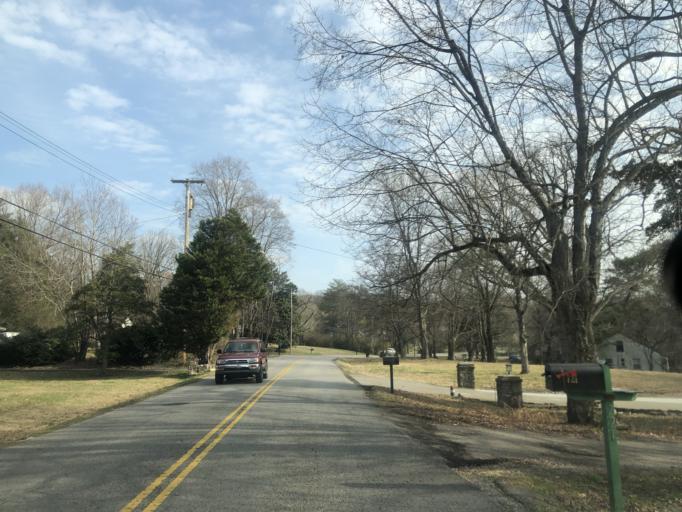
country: US
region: Tennessee
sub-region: Davidson County
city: Oak Hill
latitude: 36.1182
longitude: -86.7146
